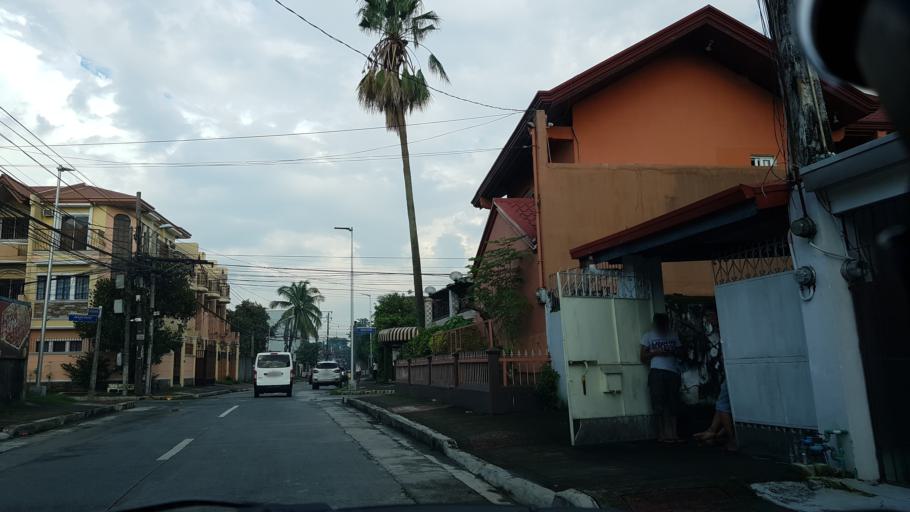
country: PH
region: Metro Manila
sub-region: Quezon City
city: Quezon City
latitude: 14.6389
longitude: 121.0599
